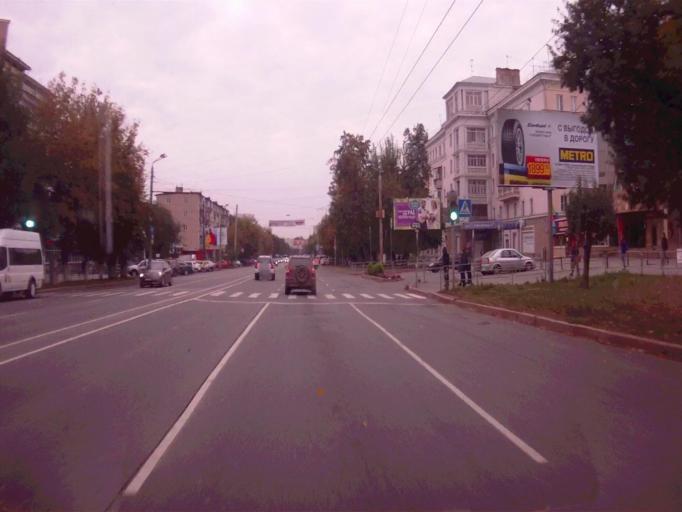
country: RU
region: Chelyabinsk
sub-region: Gorod Chelyabinsk
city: Chelyabinsk
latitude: 55.1535
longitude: 61.4144
